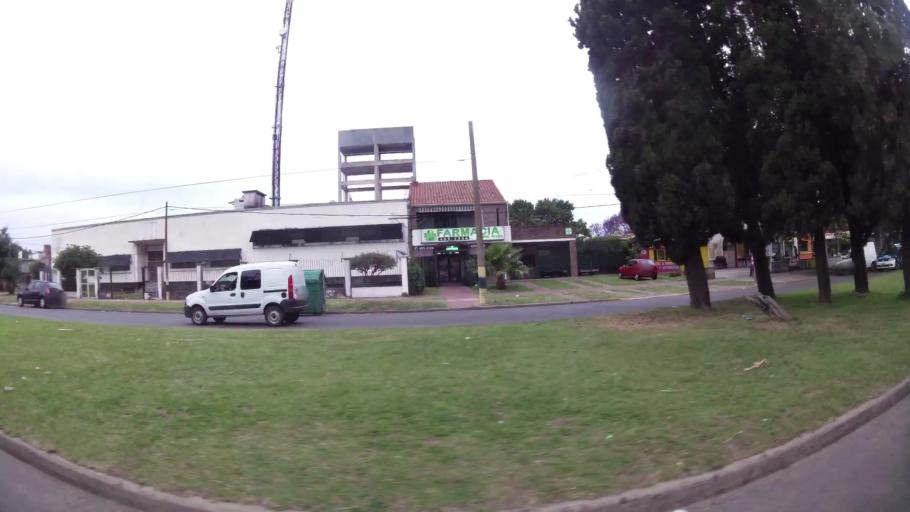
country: AR
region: Santa Fe
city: Granadero Baigorria
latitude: -32.8977
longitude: -60.6914
